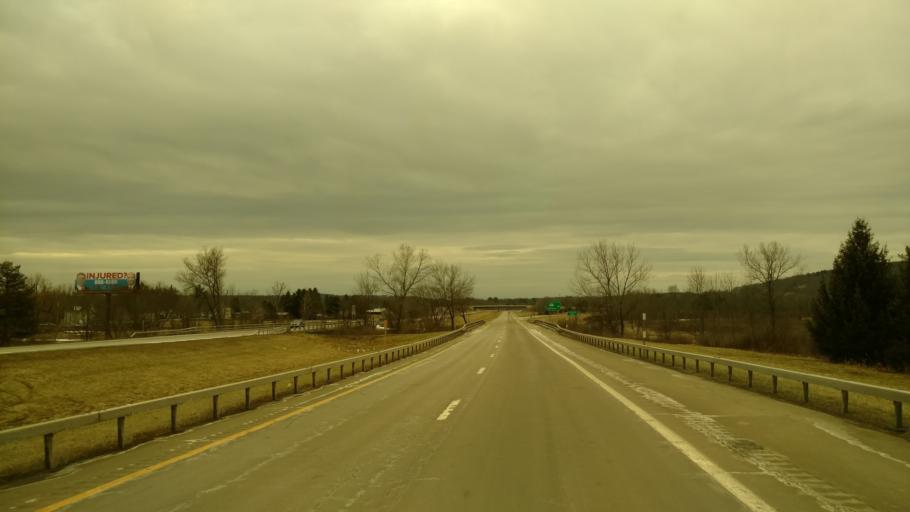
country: US
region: New York
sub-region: Chautauqua County
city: Falconer
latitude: 42.1354
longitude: -79.1820
